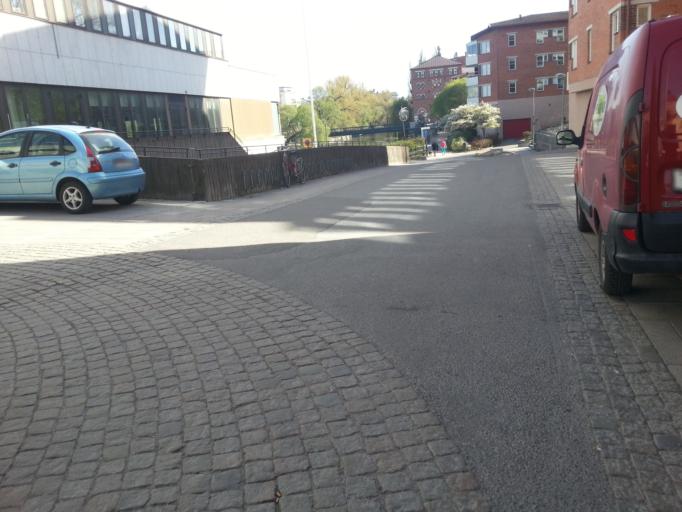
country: SE
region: OEstergoetland
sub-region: Norrkopings Kommun
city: Norrkoping
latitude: 58.5932
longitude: 16.1820
